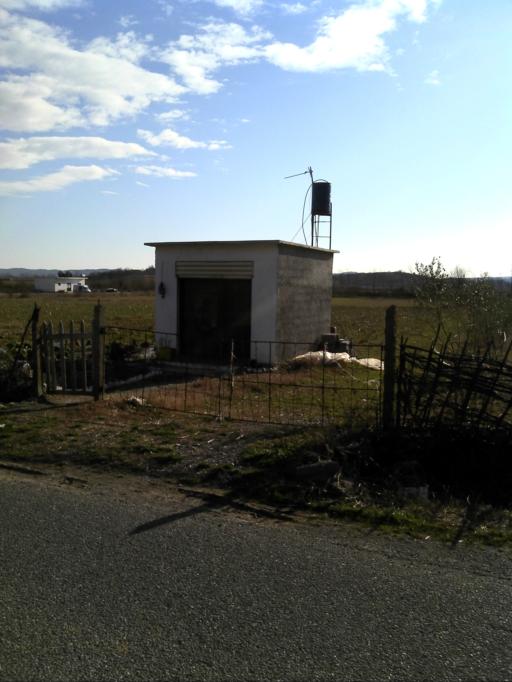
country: AL
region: Shkoder
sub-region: Rrethi i Shkodres
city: Dajc
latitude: 42.0197
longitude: 19.3829
